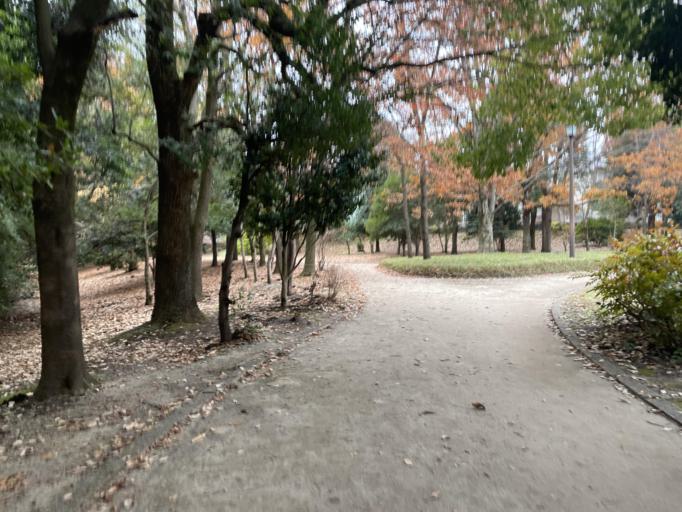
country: JP
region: Saitama
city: Shiraoka
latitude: 36.0014
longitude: 139.6584
